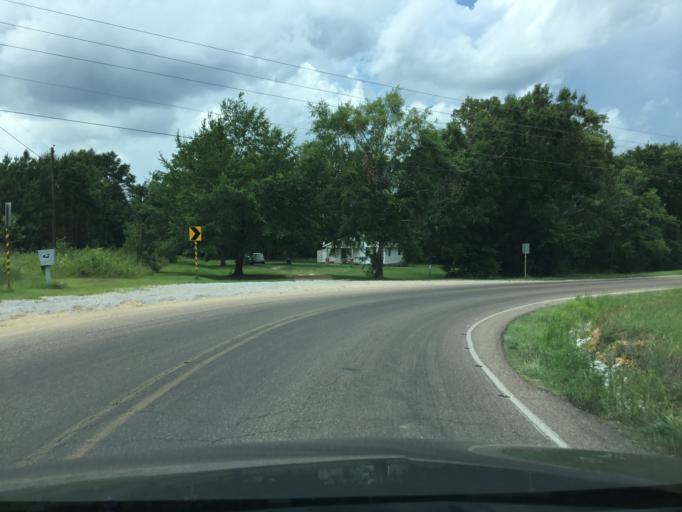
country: US
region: Alabama
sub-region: Montgomery County
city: Pike Road
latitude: 32.3642
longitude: -86.1037
